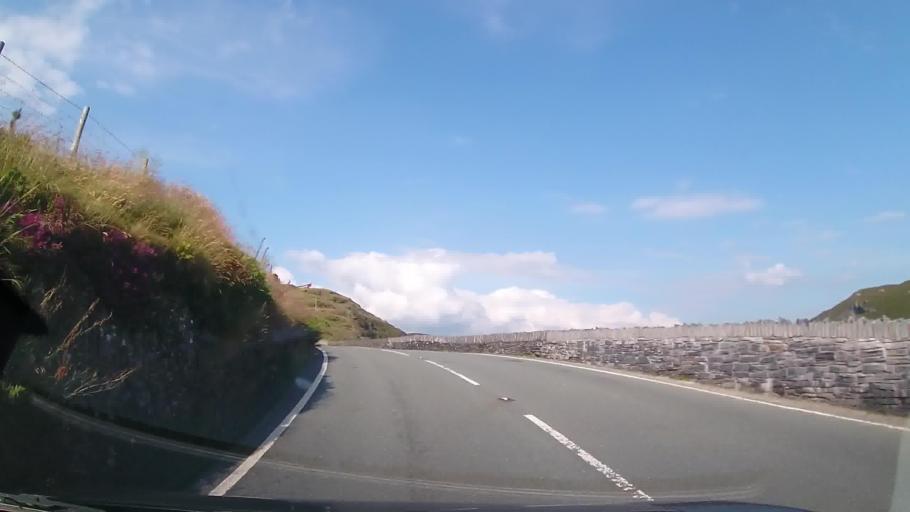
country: GB
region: Wales
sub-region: Gwynedd
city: Ffestiniog
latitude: 52.9579
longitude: -3.8834
